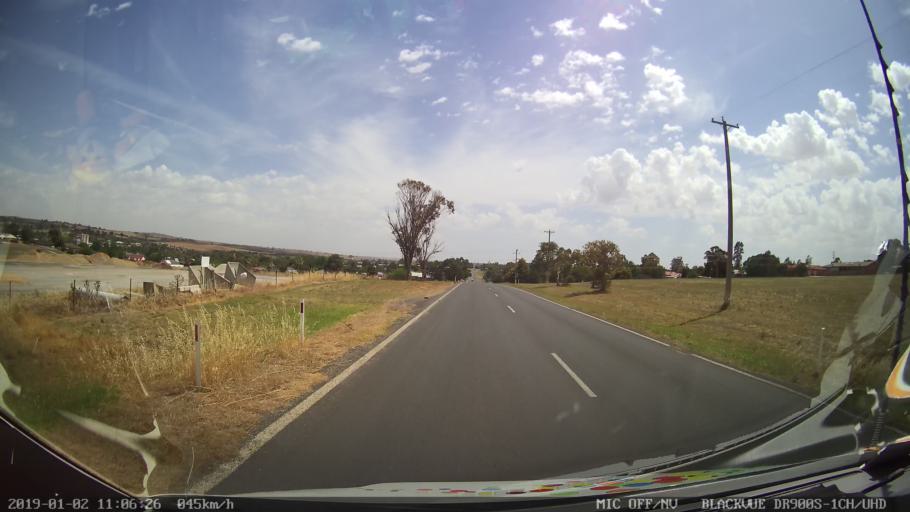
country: AU
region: New South Wales
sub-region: Young
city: Young
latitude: -34.5554
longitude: 148.3564
